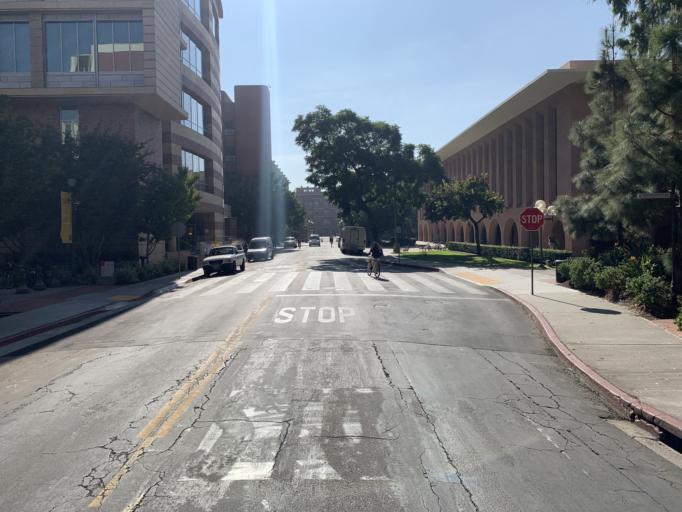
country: US
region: California
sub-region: Los Angeles County
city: Los Angeles
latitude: 34.0206
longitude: -118.2900
